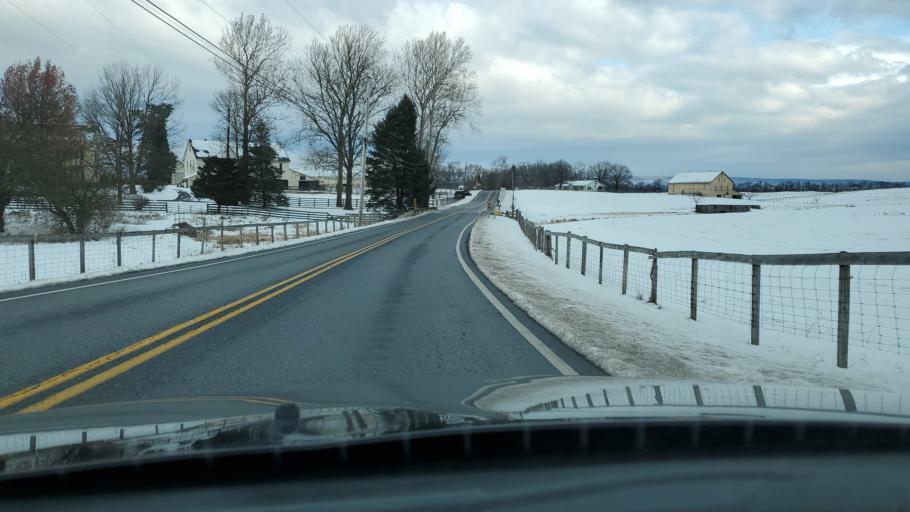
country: US
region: Pennsylvania
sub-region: Cumberland County
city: Mechanicsburg
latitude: 40.2264
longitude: -77.0549
